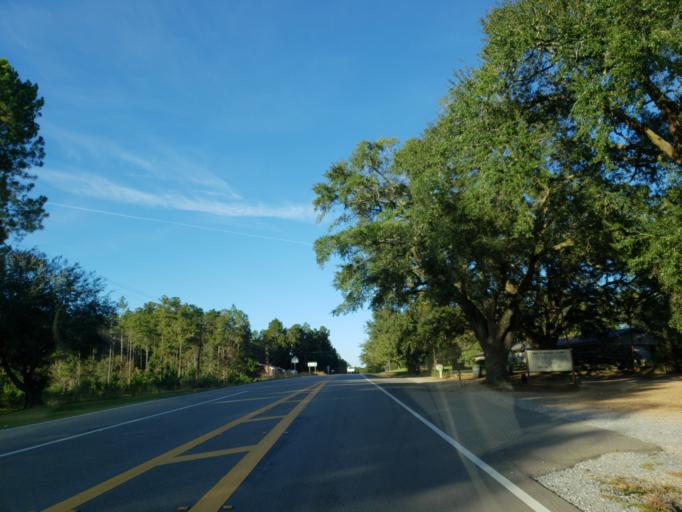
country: US
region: Mississippi
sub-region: Perry County
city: Richton
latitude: 31.3506
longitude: -88.7610
